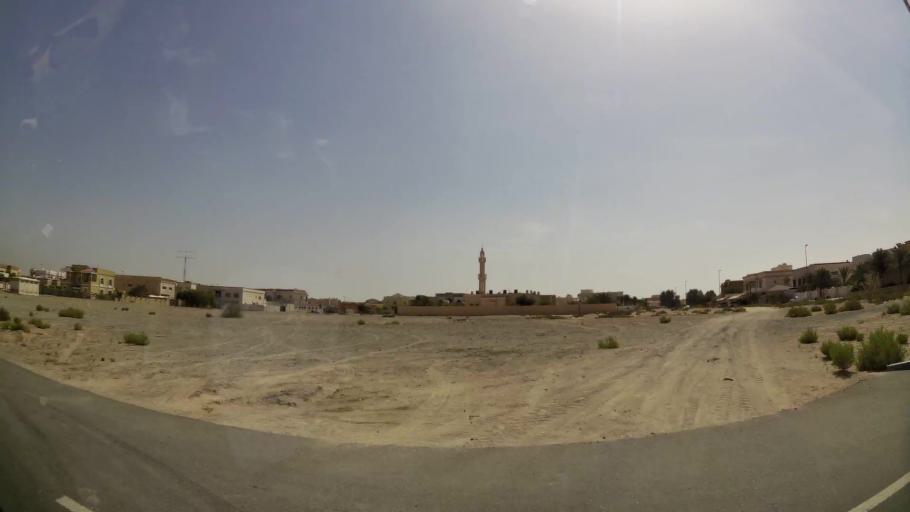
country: AE
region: Ash Shariqah
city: Sharjah
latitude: 25.2015
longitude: 55.4263
